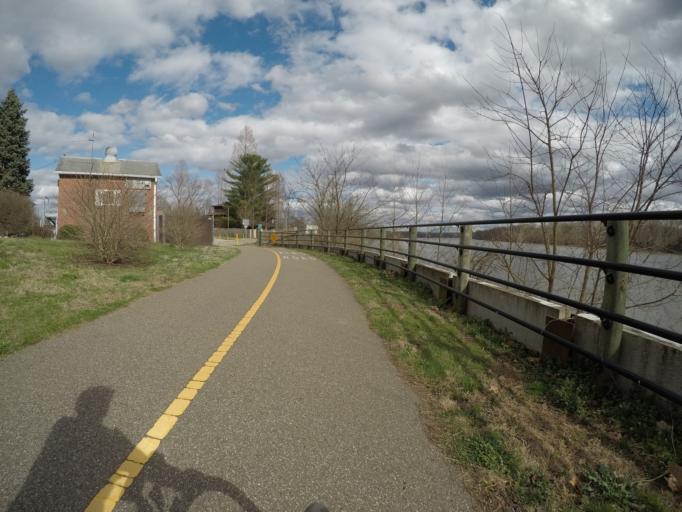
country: US
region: West Virginia
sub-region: Wood County
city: Williamstown
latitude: 39.4106
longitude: -81.4439
